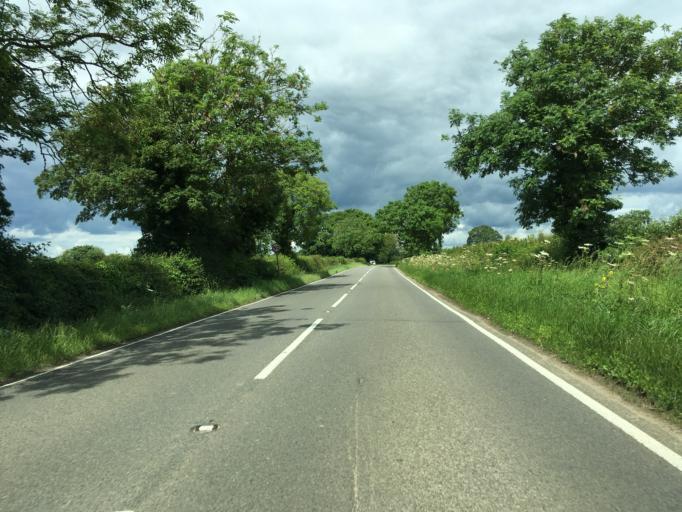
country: GB
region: England
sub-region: Northamptonshire
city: Brackley
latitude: 52.0854
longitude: -1.1852
